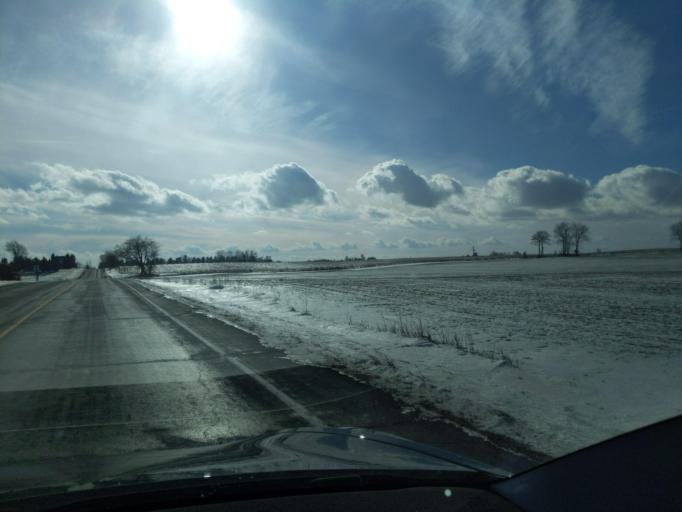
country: US
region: Michigan
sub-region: Ingham County
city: Williamston
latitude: 42.6104
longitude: -84.2797
